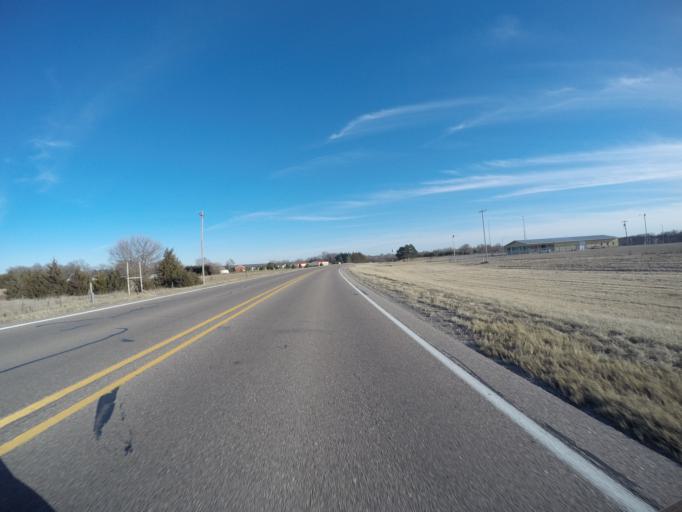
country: US
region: Nebraska
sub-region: Gage County
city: Wymore
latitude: 40.1378
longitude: -96.6753
